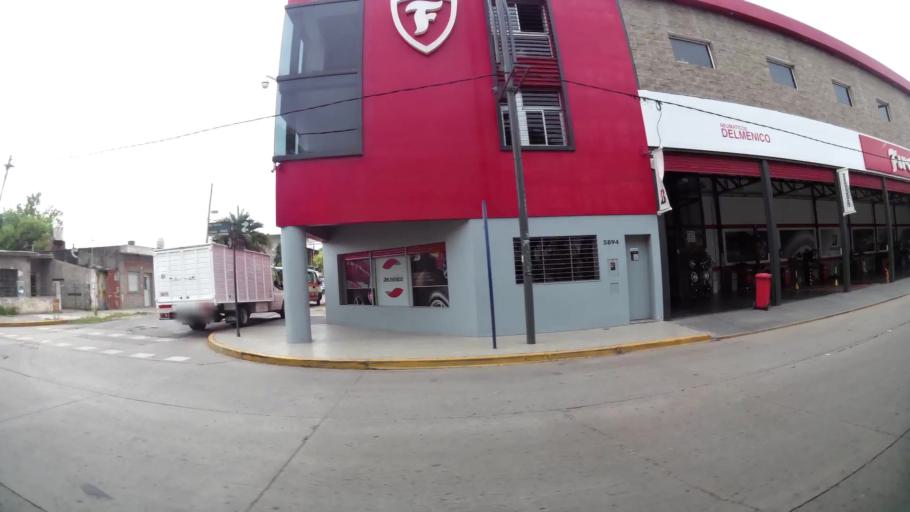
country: AR
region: Santa Fe
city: Gobernador Galvez
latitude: -33.0055
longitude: -60.6651
